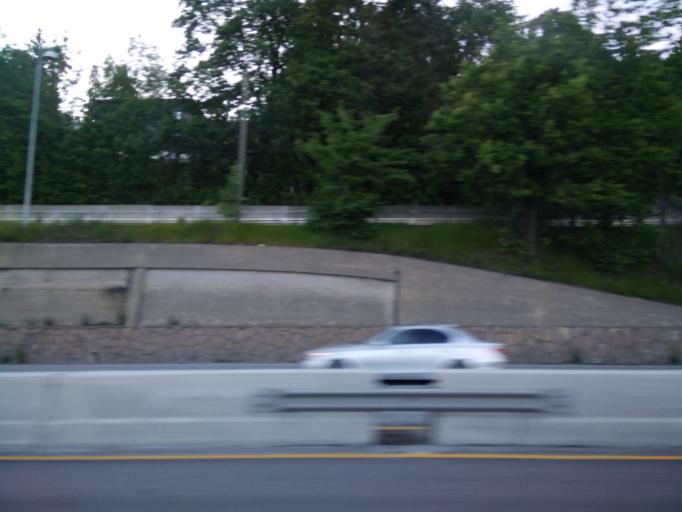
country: NO
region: Akershus
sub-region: Baerum
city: Sandvika
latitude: 59.8915
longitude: 10.5338
